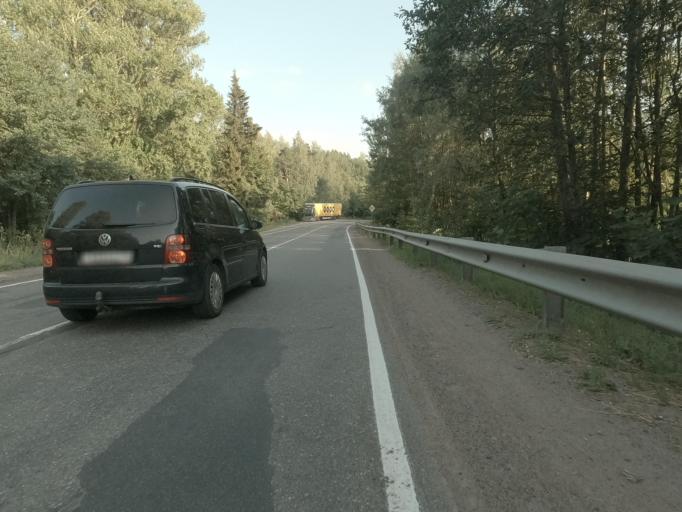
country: RU
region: Leningrad
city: Vyborg
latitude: 60.7299
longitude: 28.7595
